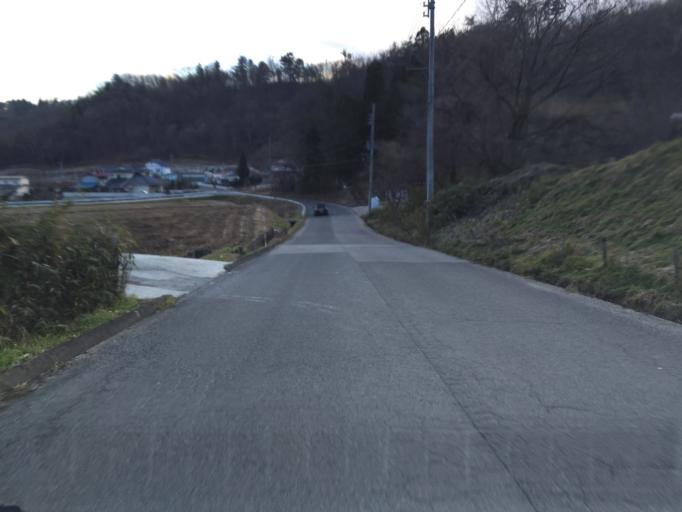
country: JP
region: Fukushima
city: Fukushima-shi
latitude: 37.7171
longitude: 140.4165
